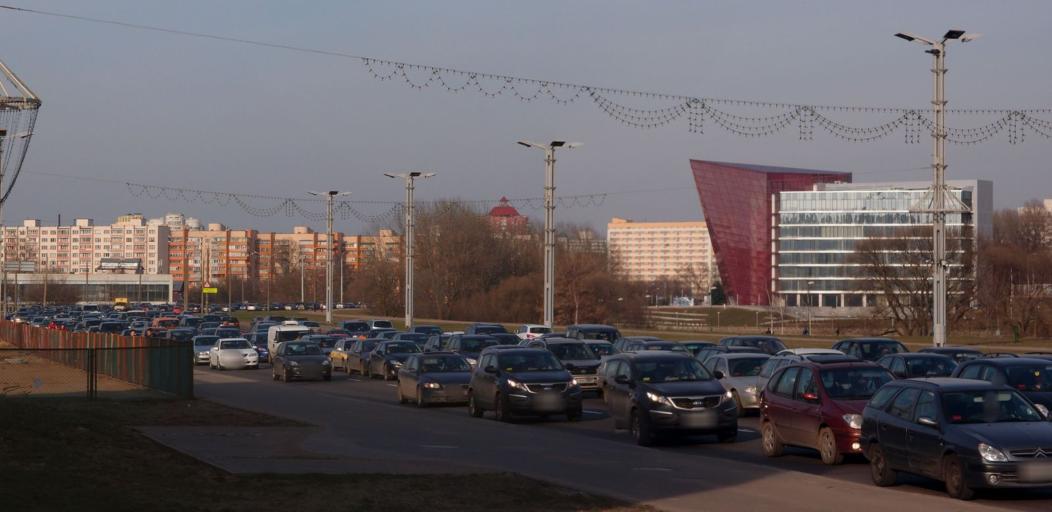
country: BY
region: Minsk
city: Minsk
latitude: 53.9145
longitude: 27.5387
